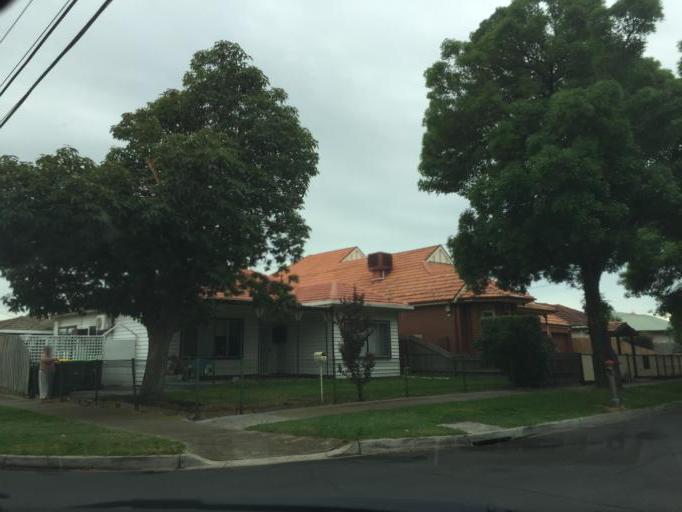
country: AU
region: Victoria
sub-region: Brimbank
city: Albion
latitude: -37.7800
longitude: 144.8386
